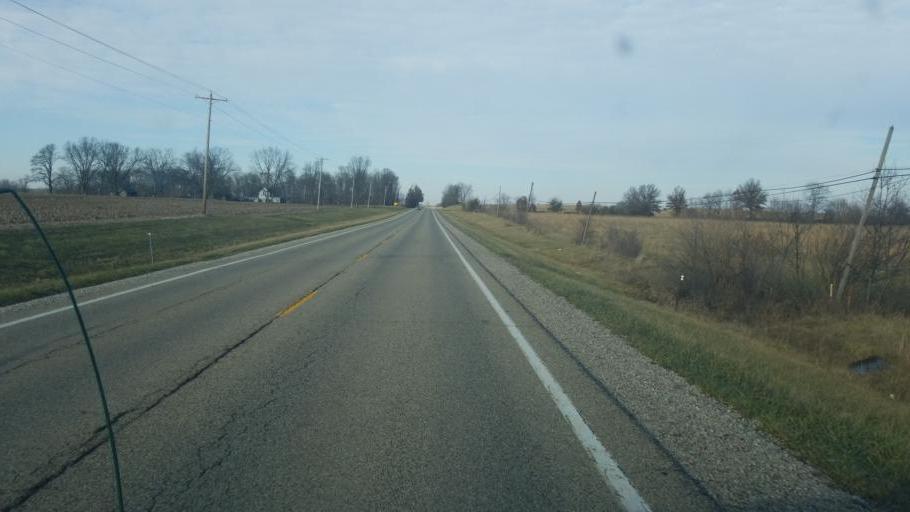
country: US
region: Illinois
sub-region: Lawrence County
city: Bridgeport
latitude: 38.6163
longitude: -87.6942
